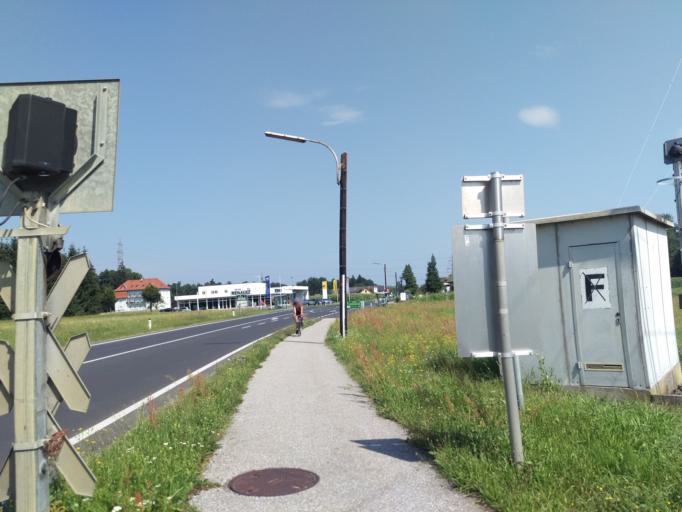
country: AT
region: Styria
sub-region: Politischer Bezirk Leibnitz
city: Weitendorf
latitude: 46.9048
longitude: 15.4818
